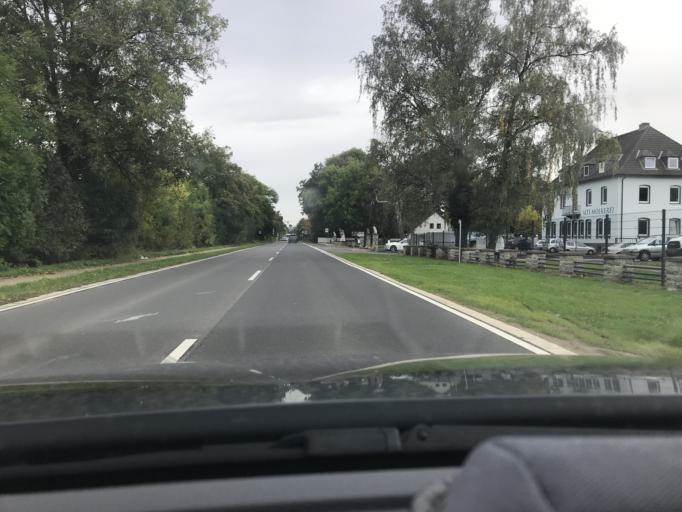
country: DE
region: North Rhine-Westphalia
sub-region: Regierungsbezirk Koln
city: Dueren
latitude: 50.8050
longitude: 6.4610
